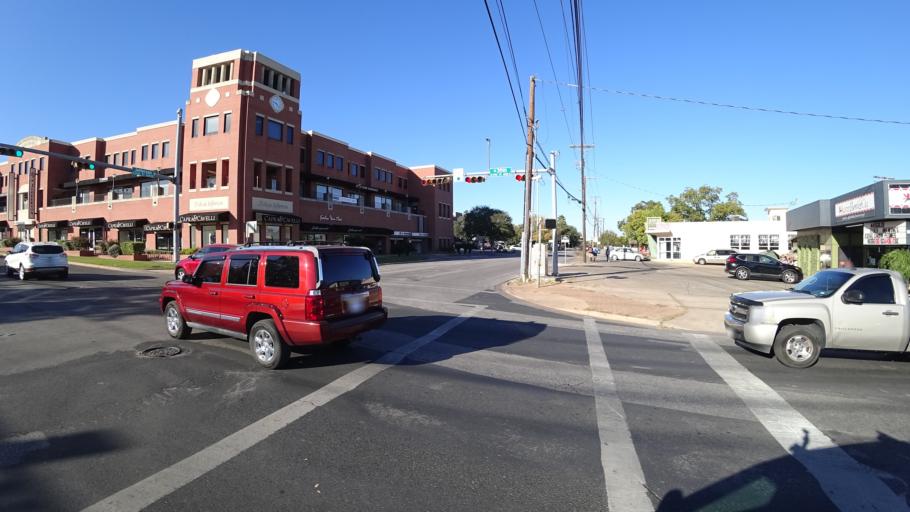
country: US
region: Texas
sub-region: Travis County
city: Austin
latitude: 30.3077
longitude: -97.7515
